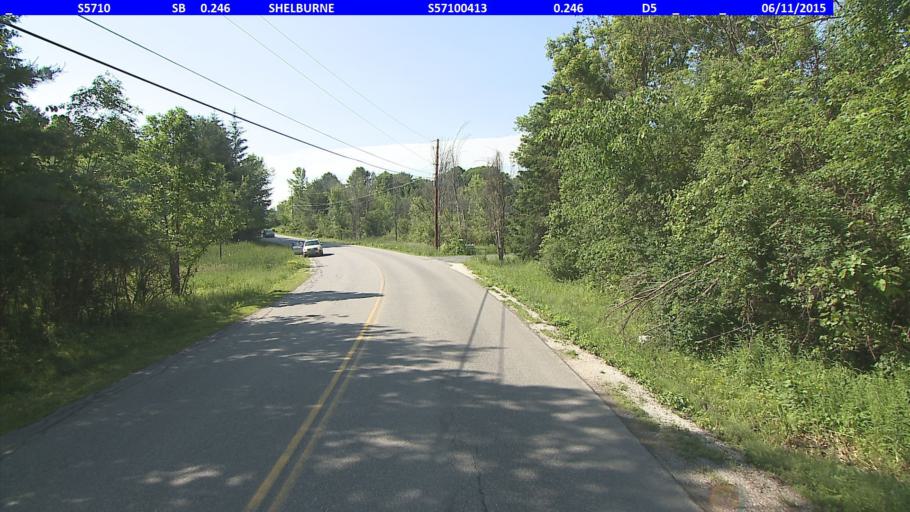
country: US
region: Vermont
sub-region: Chittenden County
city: Hinesburg
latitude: 44.3683
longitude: -73.1807
